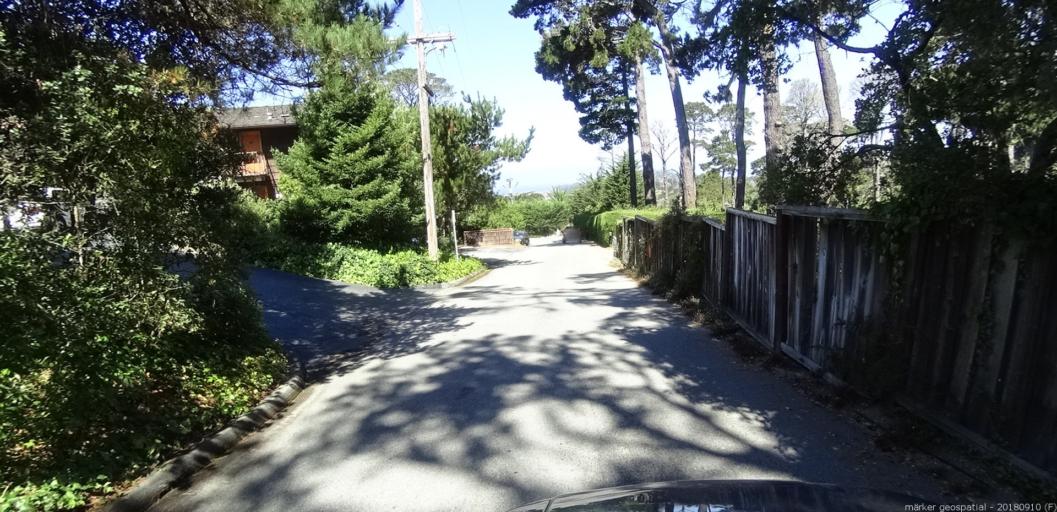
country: US
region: California
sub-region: Monterey County
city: Carmel-by-the-Sea
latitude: 36.5023
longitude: -121.9356
